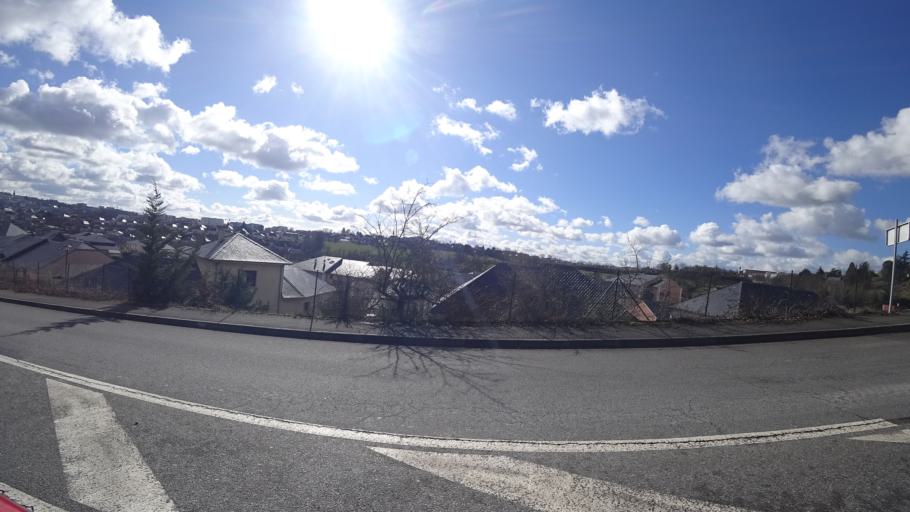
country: FR
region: Midi-Pyrenees
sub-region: Departement de l'Aveyron
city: Olemps
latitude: 44.3699
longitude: 2.5564
